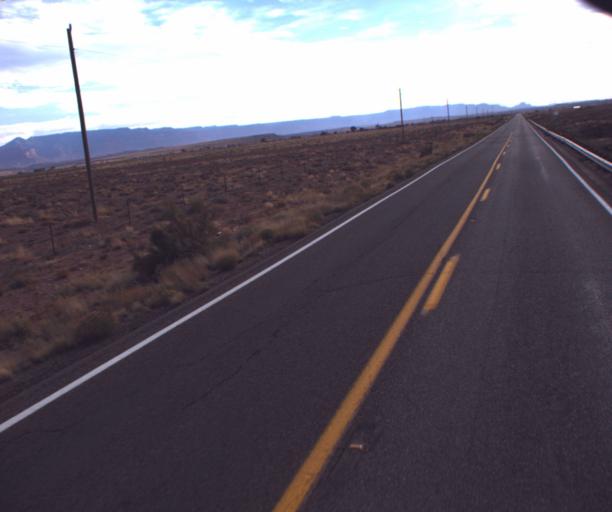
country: US
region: Arizona
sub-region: Apache County
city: Many Farms
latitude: 36.5238
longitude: -109.4961
